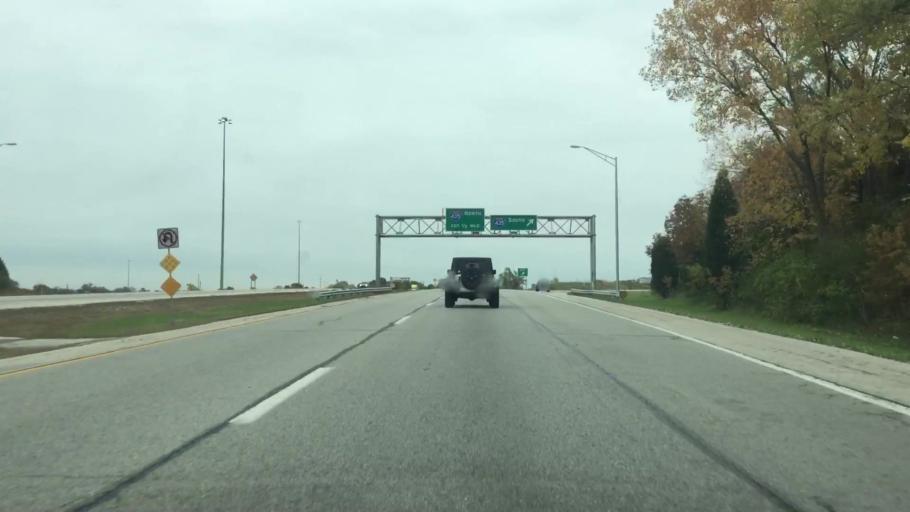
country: US
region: Kansas
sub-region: Wyandotte County
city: Edwardsville
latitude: 39.0104
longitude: -94.7915
